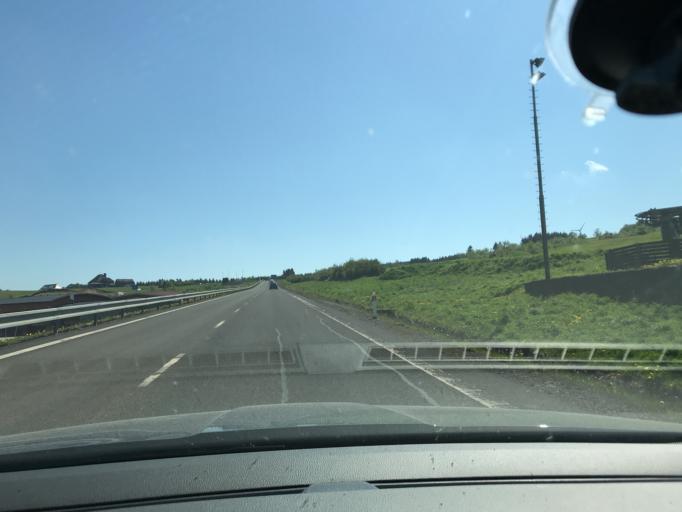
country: DE
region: Saxony
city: Kurort Oberwiesenthal
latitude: 50.4085
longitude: 12.9261
